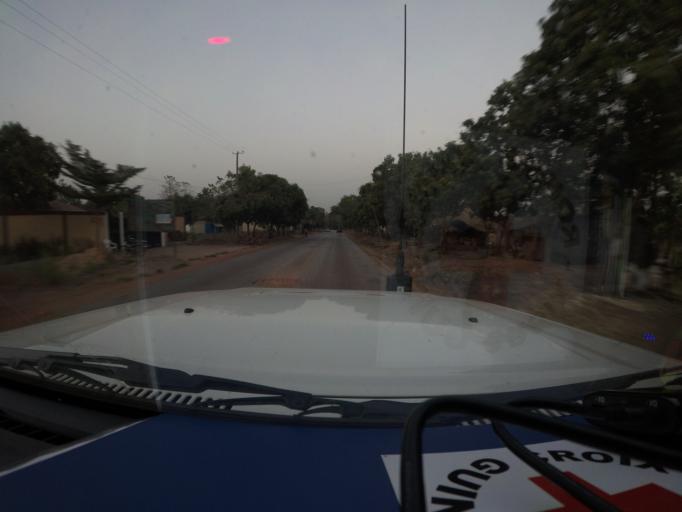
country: GN
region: Kindia
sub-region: Kindia
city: Kindia
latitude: 9.9238
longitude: -12.9930
